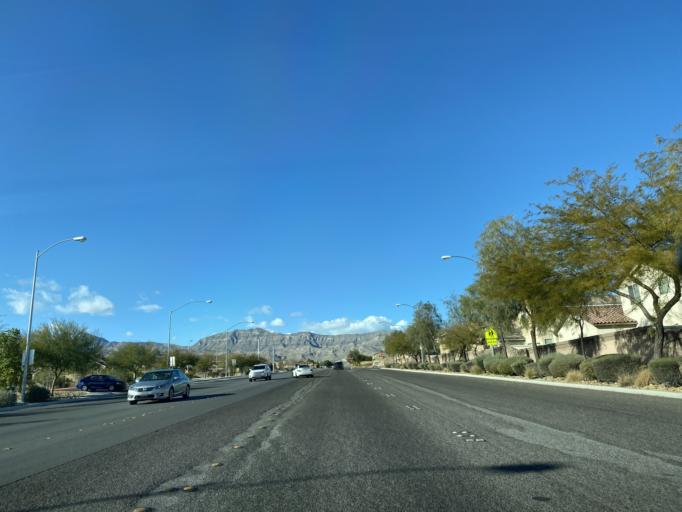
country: US
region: Nevada
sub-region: Clark County
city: Summerlin South
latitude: 36.2773
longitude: -115.2951
